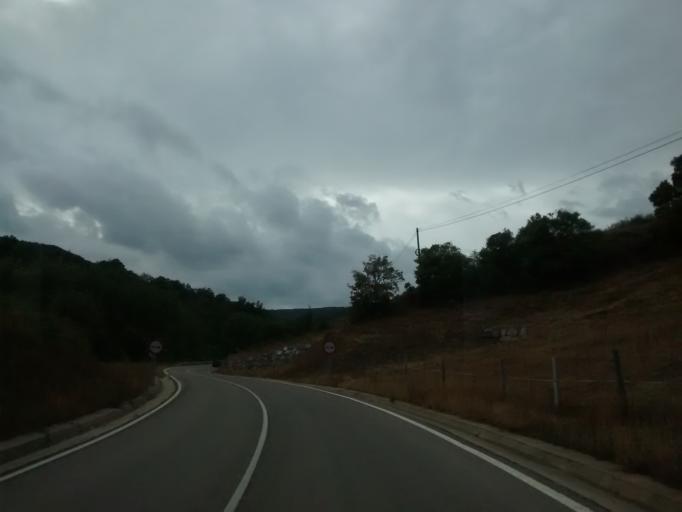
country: ES
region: Castille and Leon
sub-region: Provincia de Palencia
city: Berzosilla
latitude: 42.8609
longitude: -4.0461
